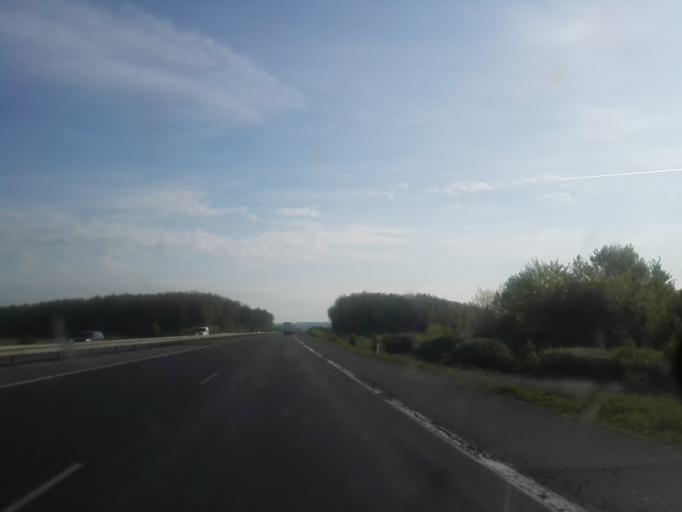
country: PL
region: Lodz Voivodeship
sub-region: Powiat piotrkowski
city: Wola Krzysztoporska
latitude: 51.2986
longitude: 19.5509
